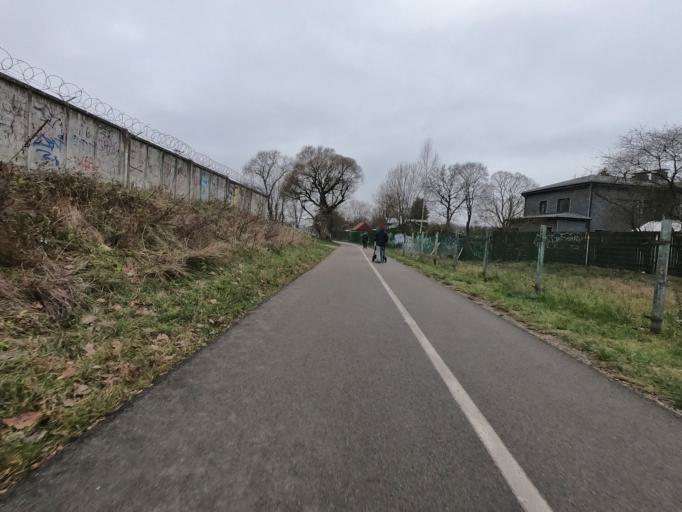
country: LV
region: Marupe
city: Marupe
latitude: 56.9490
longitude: 24.0264
